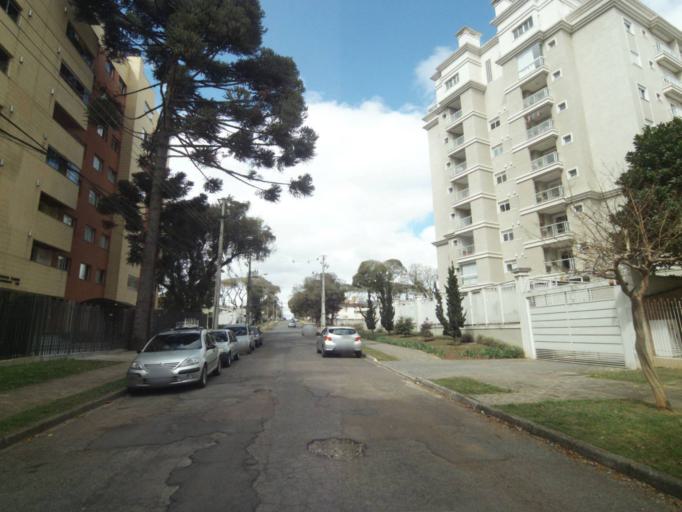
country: BR
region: Parana
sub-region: Curitiba
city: Curitiba
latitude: -25.4637
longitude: -49.2806
